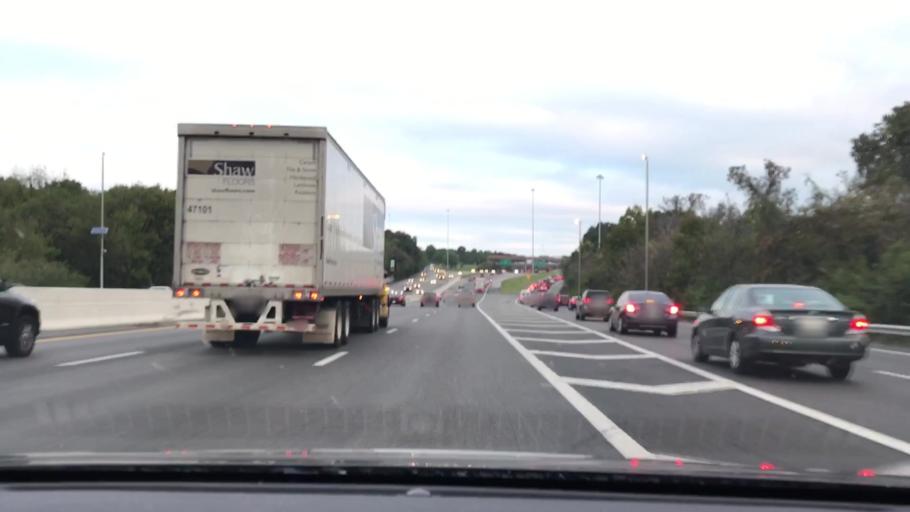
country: US
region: Tennessee
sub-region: Davidson County
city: Oak Hill
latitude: 36.1189
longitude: -86.7262
